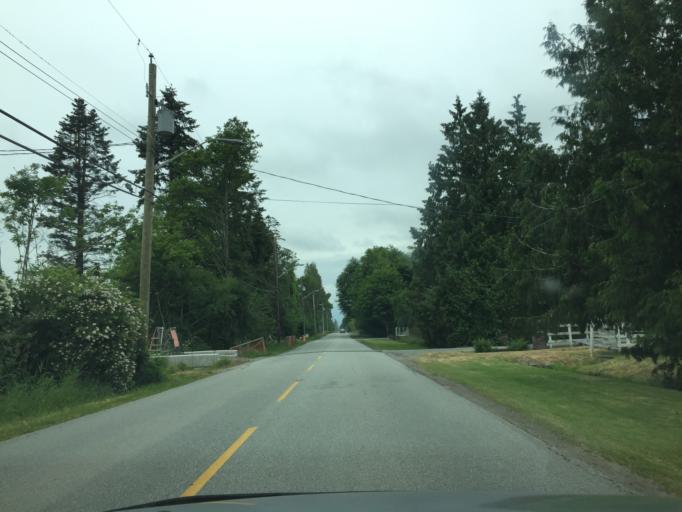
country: CA
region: British Columbia
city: Ladner
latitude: 49.1392
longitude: -123.0808
